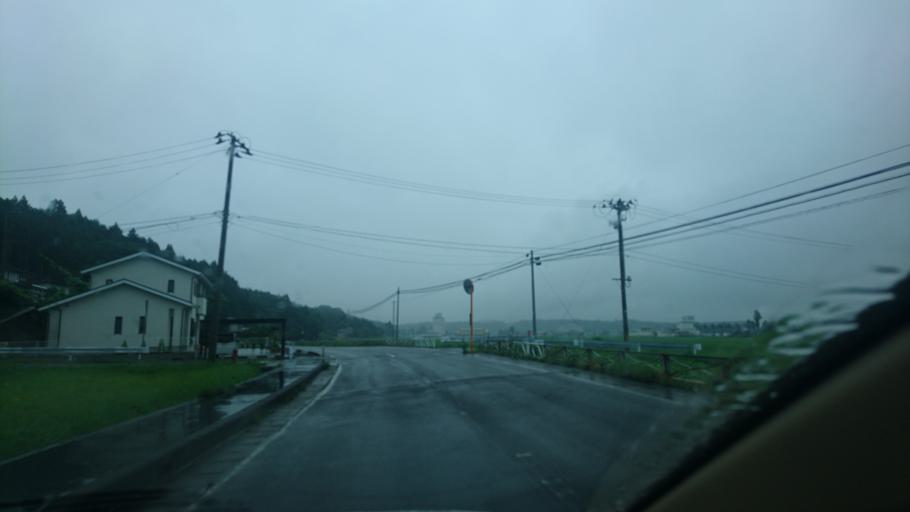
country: JP
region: Iwate
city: Kitakami
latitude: 39.2177
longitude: 141.1456
